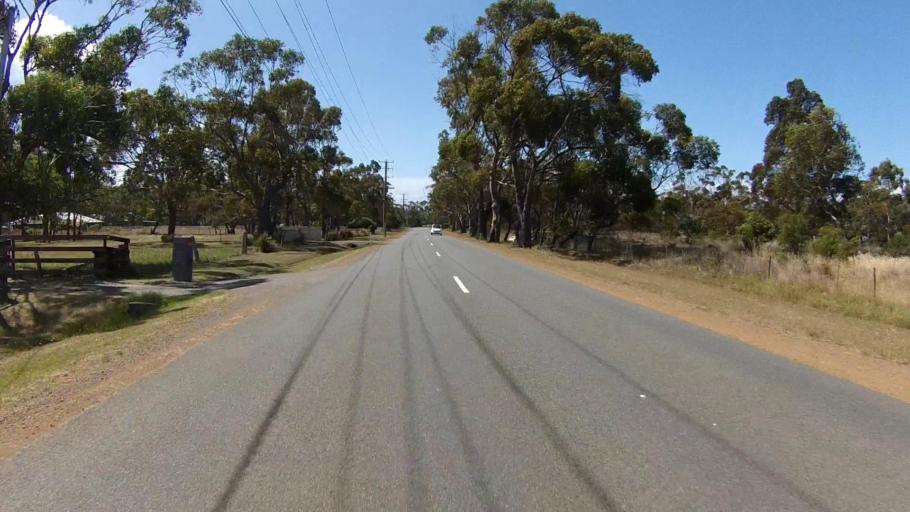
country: AU
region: Tasmania
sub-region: Clarence
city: Sandford
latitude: -42.9489
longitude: 147.4815
